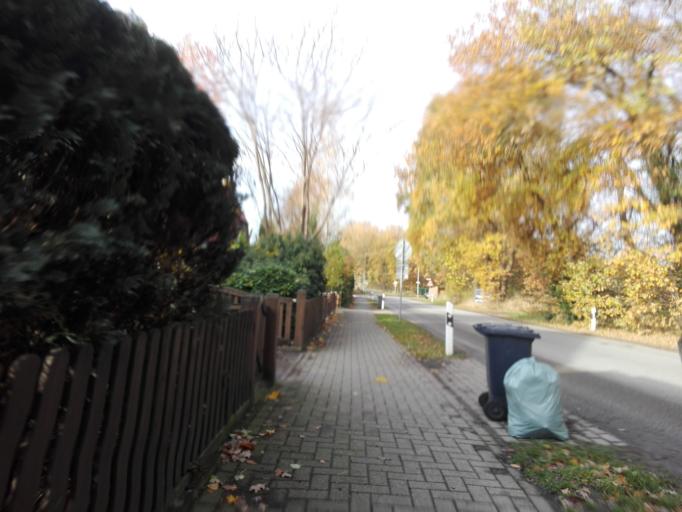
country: DE
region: Lower Saxony
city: Wiefelstede
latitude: 53.2856
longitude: 8.1351
